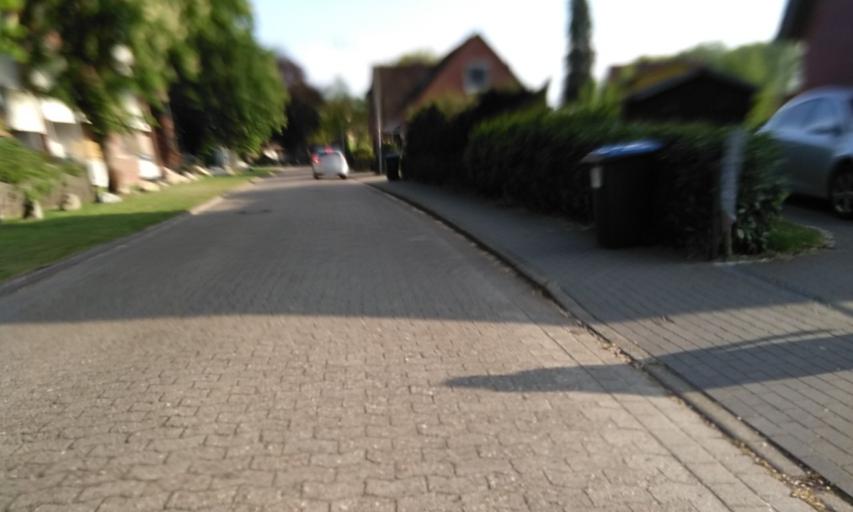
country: DE
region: Lower Saxony
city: Horneburg
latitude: 53.5037
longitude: 9.5749
